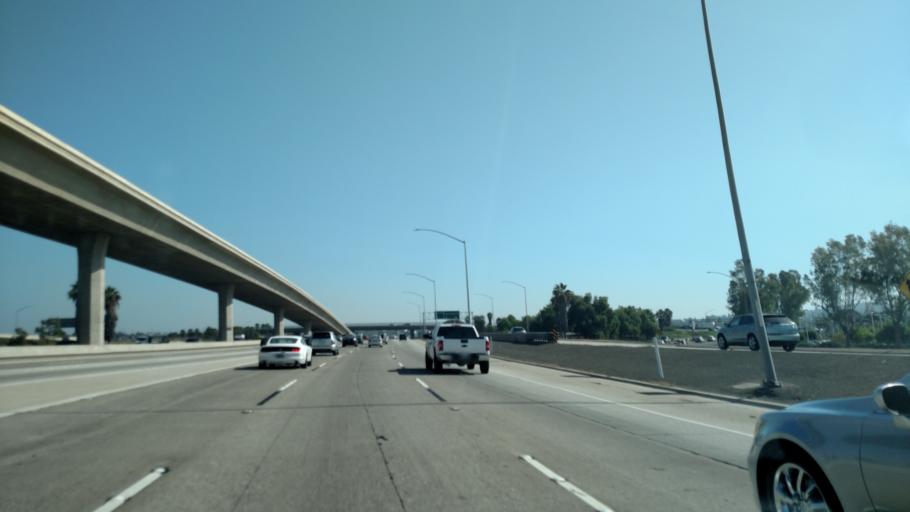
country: US
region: California
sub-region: Orange County
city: Laguna Woods
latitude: 33.6426
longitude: -117.7339
